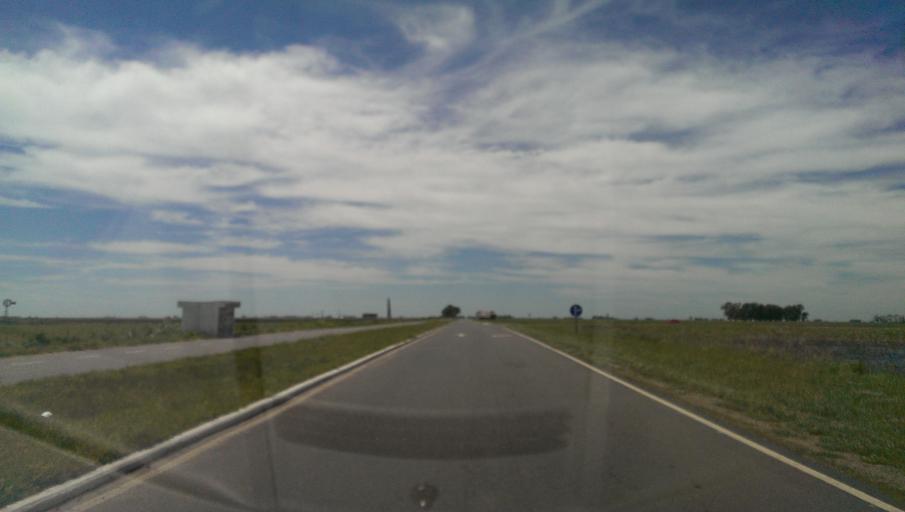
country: AR
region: Buenos Aires
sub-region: Partido de General La Madrid
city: General La Madrid
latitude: -37.4273
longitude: -61.0712
